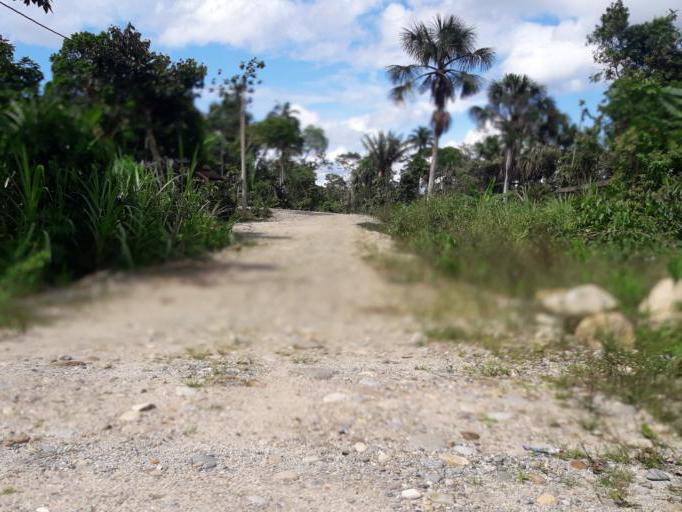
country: EC
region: Napo
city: Tena
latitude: -0.9567
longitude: -77.8189
